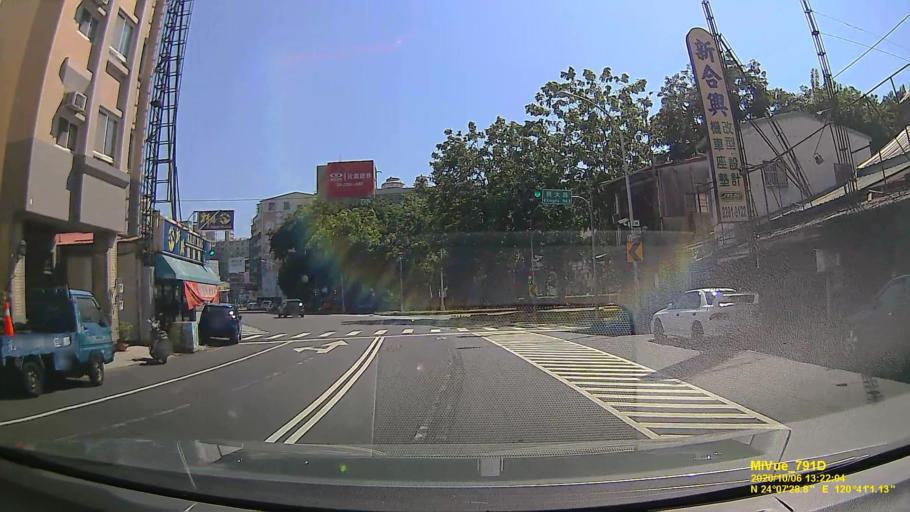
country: TW
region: Taiwan
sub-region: Taichung City
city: Taichung
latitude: 24.1247
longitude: 120.6836
